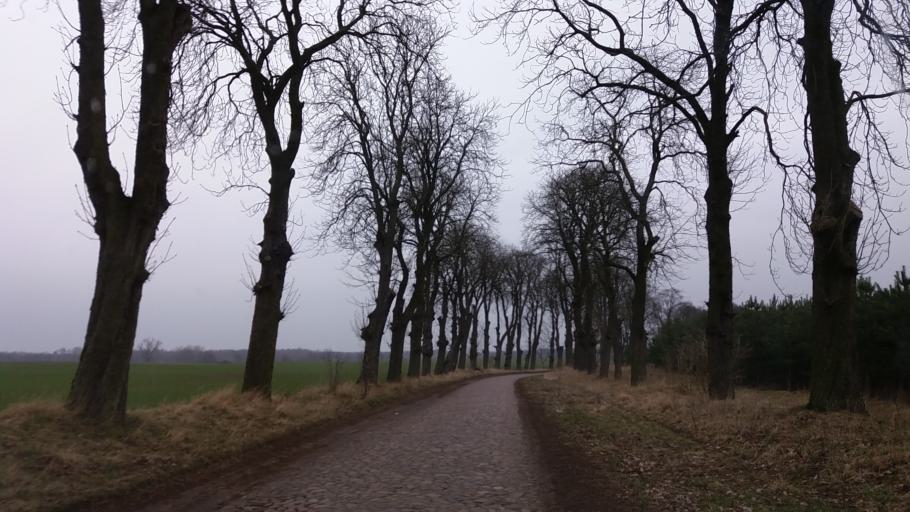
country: PL
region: West Pomeranian Voivodeship
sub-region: Powiat choszczenski
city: Choszczno
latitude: 53.1810
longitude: 15.3282
